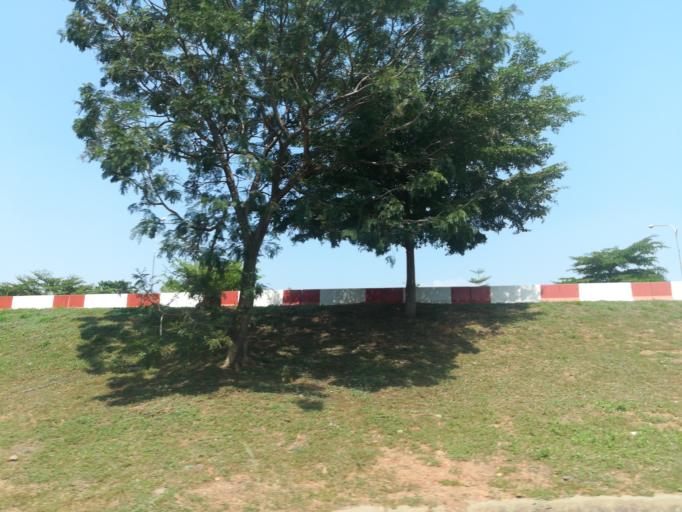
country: NG
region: Abuja Federal Capital Territory
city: Abuja
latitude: 9.0758
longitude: 7.4405
